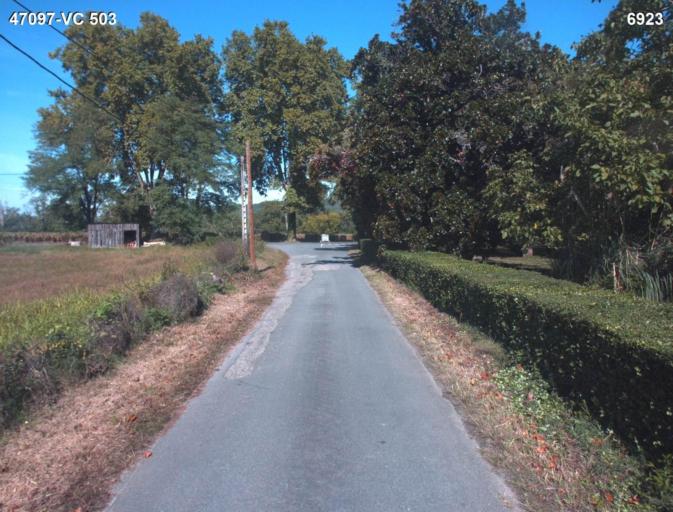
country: FR
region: Aquitaine
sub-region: Departement du Lot-et-Garonne
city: Port-Sainte-Marie
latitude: 44.2436
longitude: 0.3833
